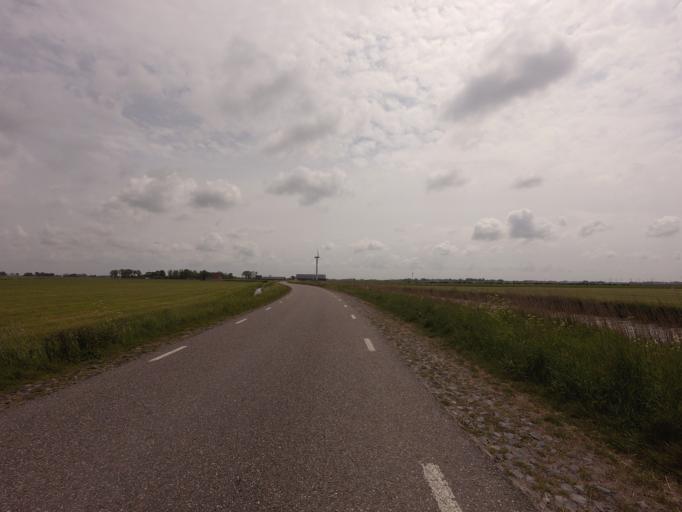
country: NL
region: Friesland
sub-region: Sudwest Fryslan
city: Bolsward
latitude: 53.1018
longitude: 5.5143
